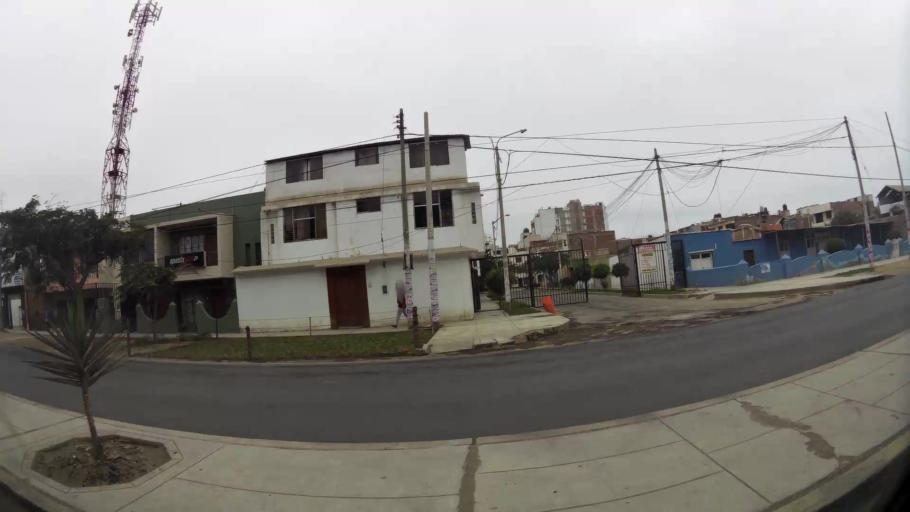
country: PE
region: La Libertad
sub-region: Provincia de Trujillo
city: Buenos Aires
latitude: -8.1326
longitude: -79.0457
